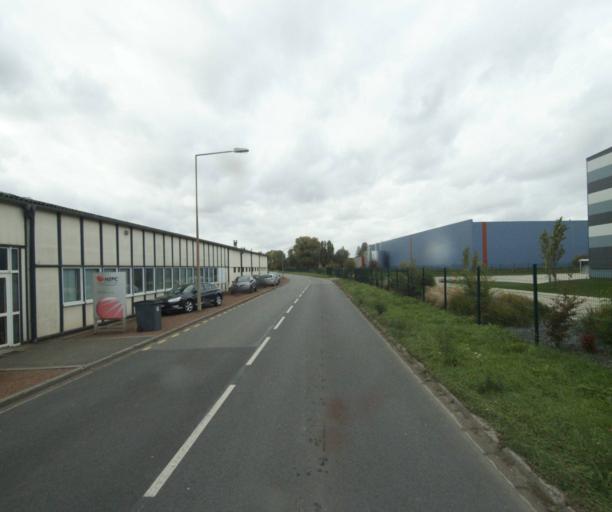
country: FR
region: Nord-Pas-de-Calais
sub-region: Departement du Nord
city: Radinghem-en-Weppes
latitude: 50.6504
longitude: 2.9099
